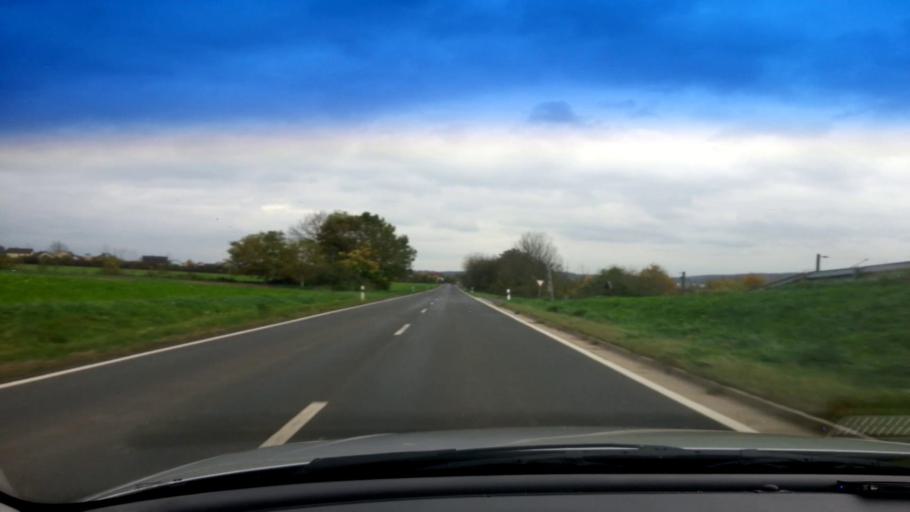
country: DE
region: Bavaria
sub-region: Regierungsbezirk Unterfranken
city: Stettfeld
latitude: 49.9509
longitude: 10.7427
